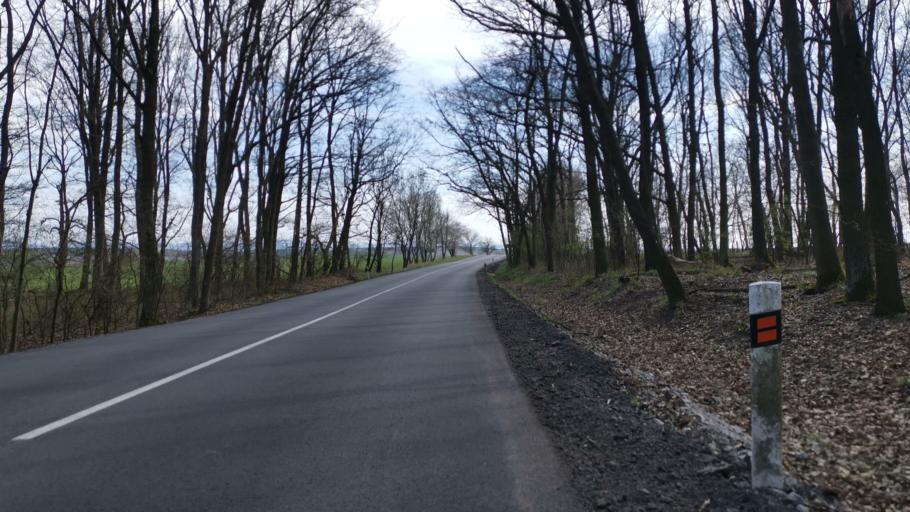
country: SK
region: Trnavsky
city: Gbely
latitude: 48.6951
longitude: 17.1261
